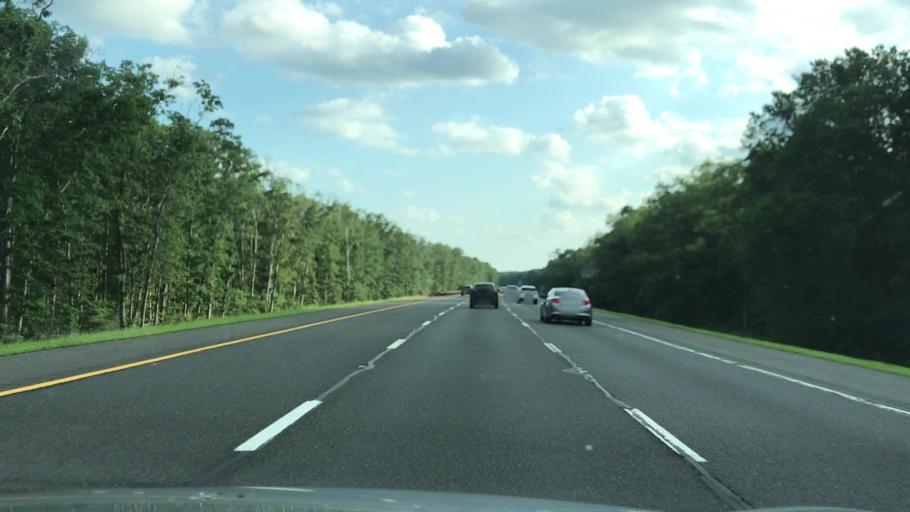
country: US
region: New Jersey
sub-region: Ocean County
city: Ocean Acres
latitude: 39.7369
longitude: -74.2612
